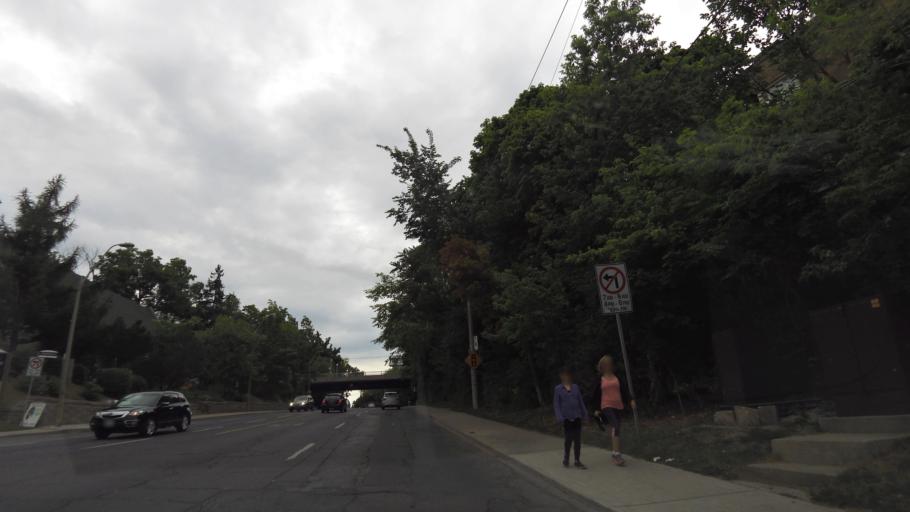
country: CA
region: Ontario
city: Toronto
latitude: 43.7015
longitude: -79.4256
